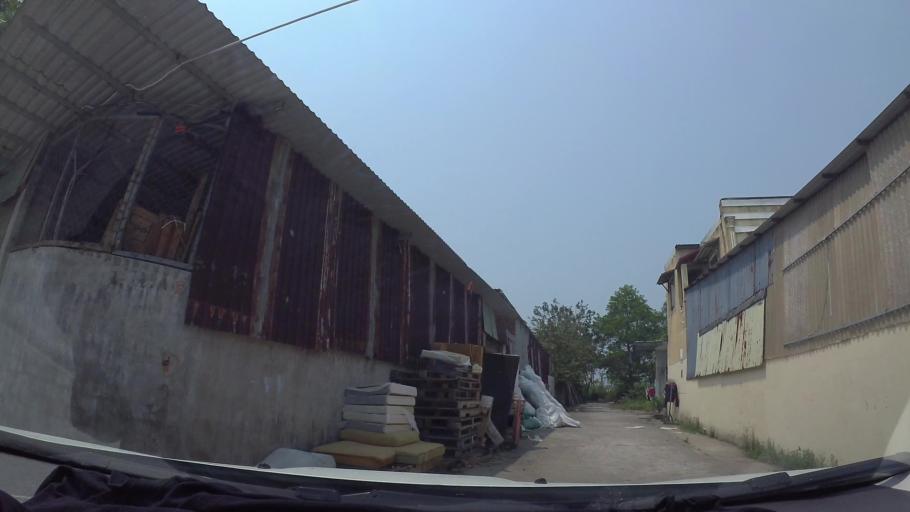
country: VN
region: Da Nang
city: Cam Le
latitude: 15.9912
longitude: 108.2069
